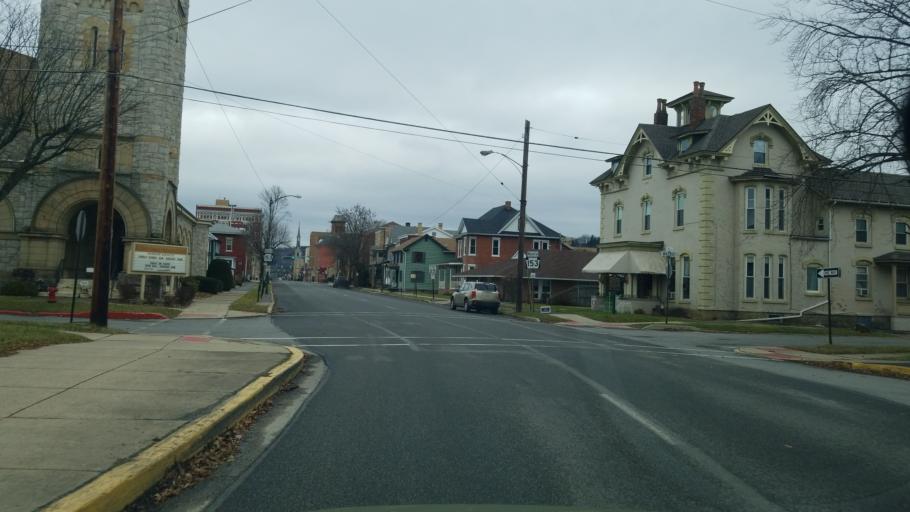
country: US
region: Pennsylvania
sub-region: Clearfield County
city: Clearfield
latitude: 41.0195
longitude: -78.4381
